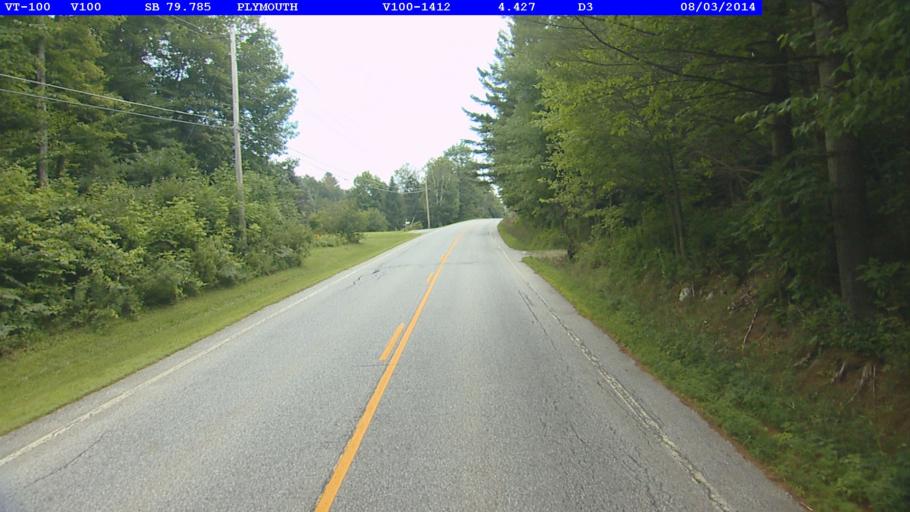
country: US
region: Vermont
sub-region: Windsor County
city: Woodstock
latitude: 43.5185
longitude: -72.7323
